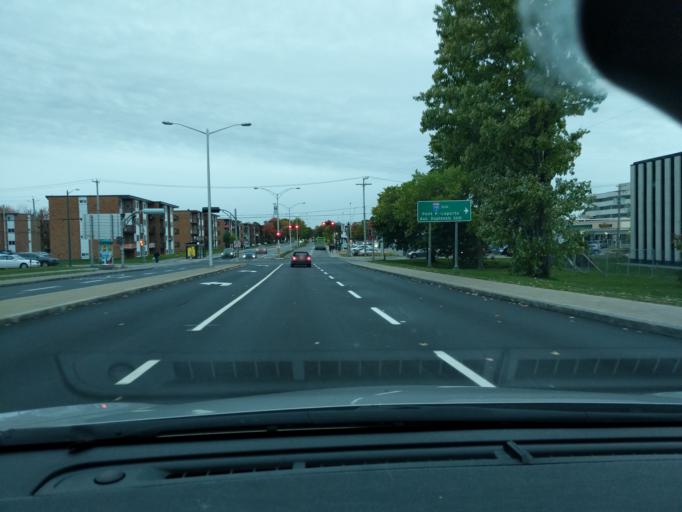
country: CA
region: Quebec
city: L'Ancienne-Lorette
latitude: 46.7640
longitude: -71.3154
